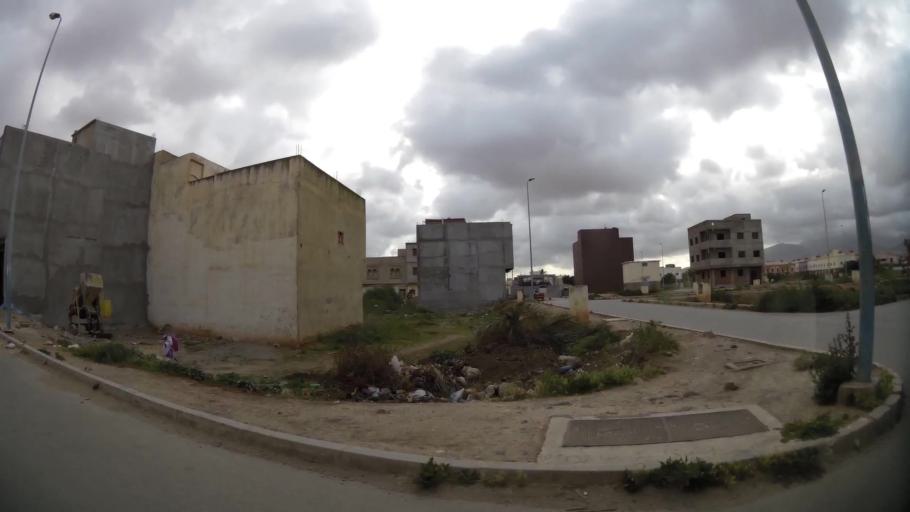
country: MA
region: Oriental
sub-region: Nador
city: Nador
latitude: 35.1591
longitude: -2.9144
